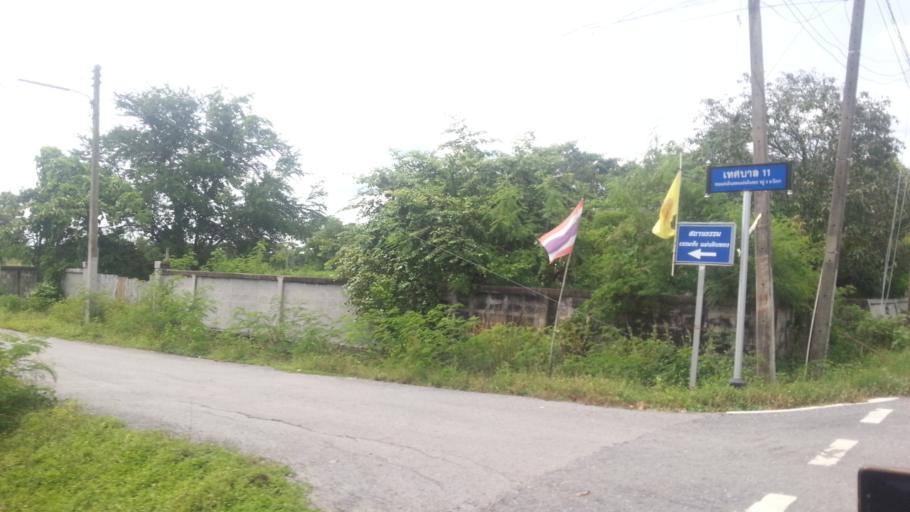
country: TH
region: Pathum Thani
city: Nong Suea
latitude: 14.1119
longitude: 100.8236
